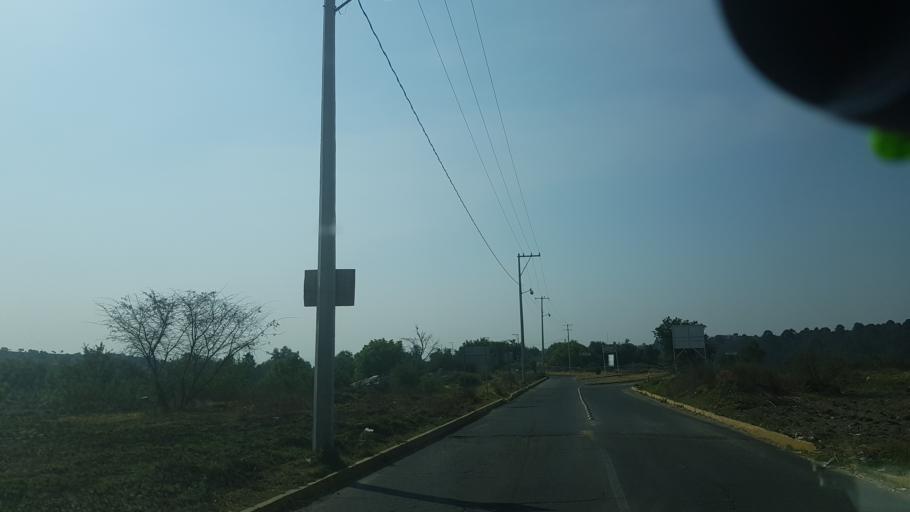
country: MX
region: Puebla
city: San Nicolas de los Ranchos
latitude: 19.0640
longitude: -98.4721
